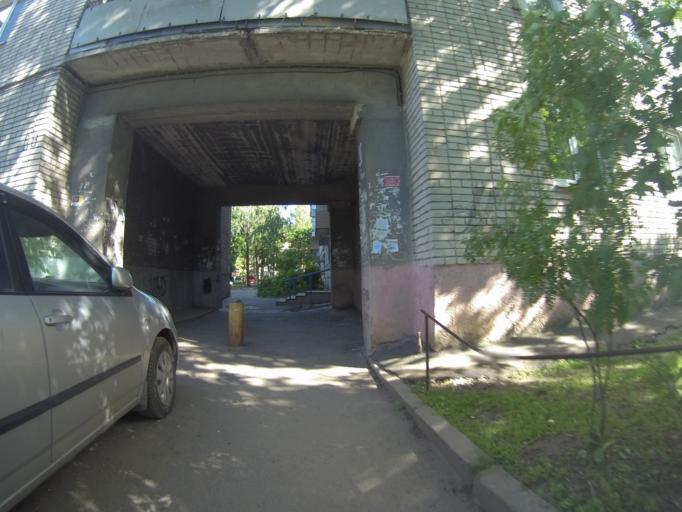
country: RU
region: Vladimir
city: Bogolyubovo
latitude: 56.1706
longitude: 40.4804
